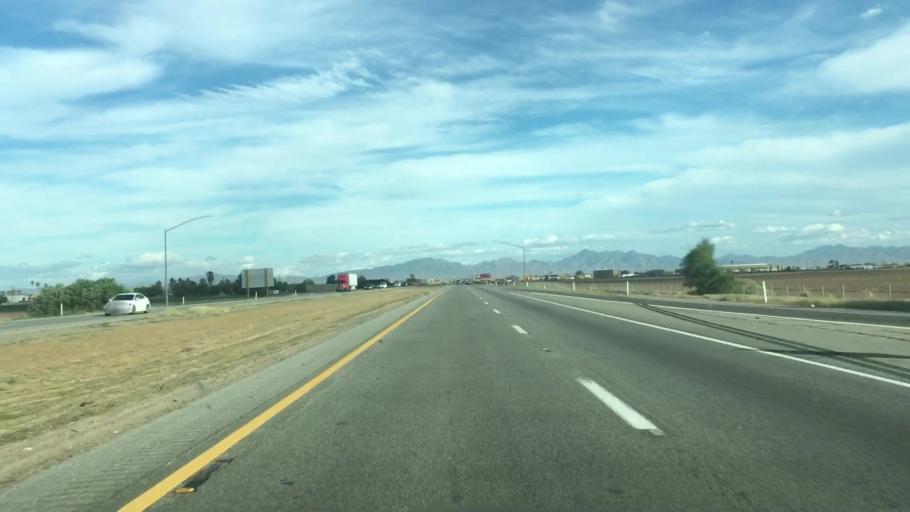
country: US
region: California
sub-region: Riverside County
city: Blythe
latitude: 33.6065
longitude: -114.6552
